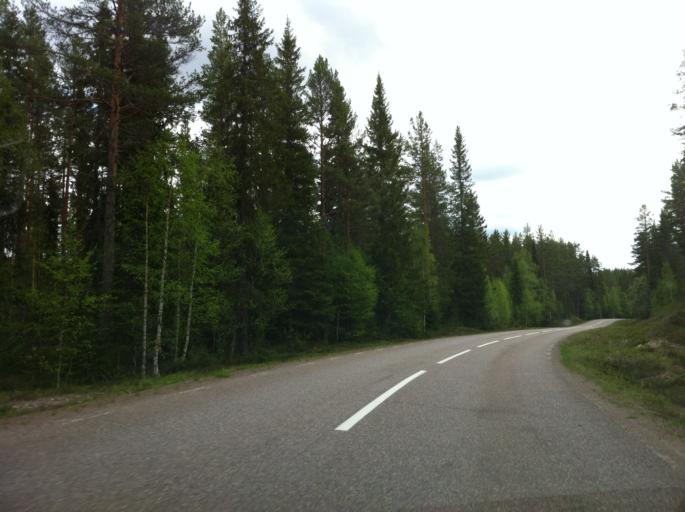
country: NO
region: Hedmark
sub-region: Trysil
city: Innbygda
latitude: 61.3646
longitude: 13.0572
